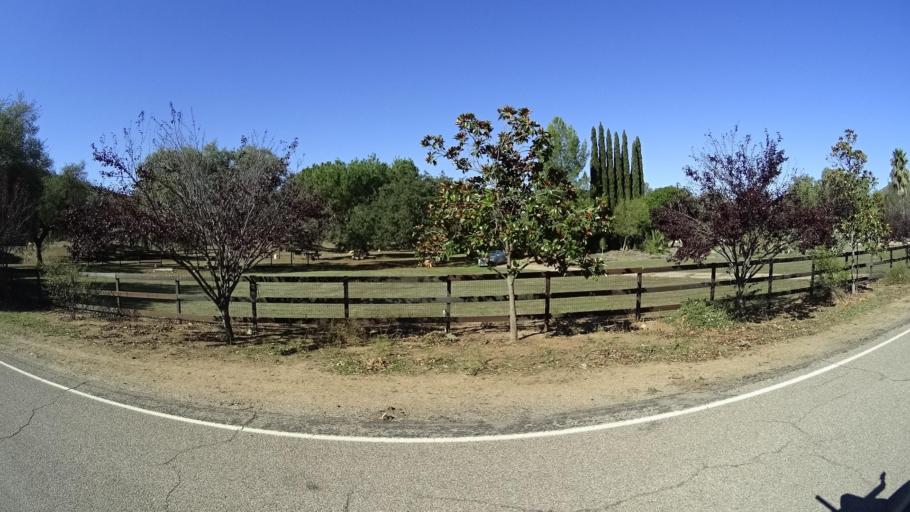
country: US
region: California
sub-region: San Diego County
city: Jamul
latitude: 32.7179
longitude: -116.8034
